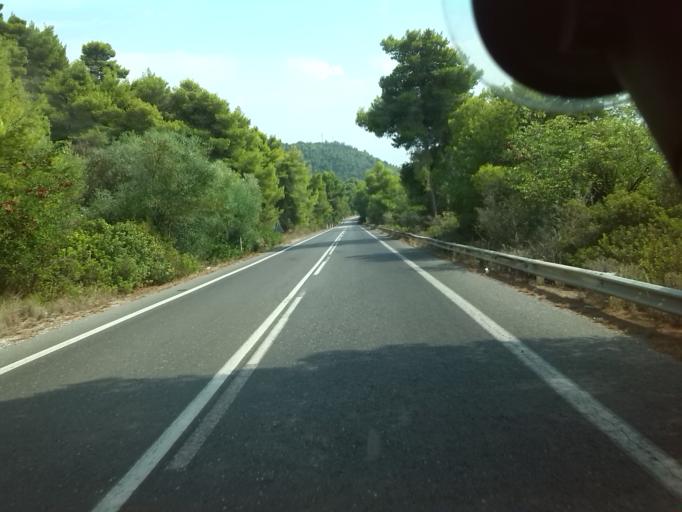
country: GR
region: West Greece
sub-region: Nomos Ileias
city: Zacharo
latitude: 37.3726
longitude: 21.6914
